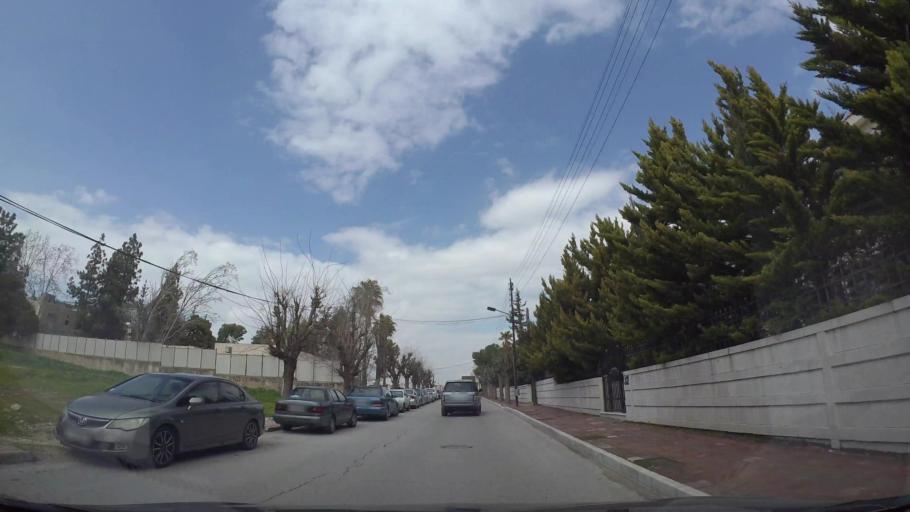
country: JO
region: Amman
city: Amman
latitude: 31.9744
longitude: 35.8990
